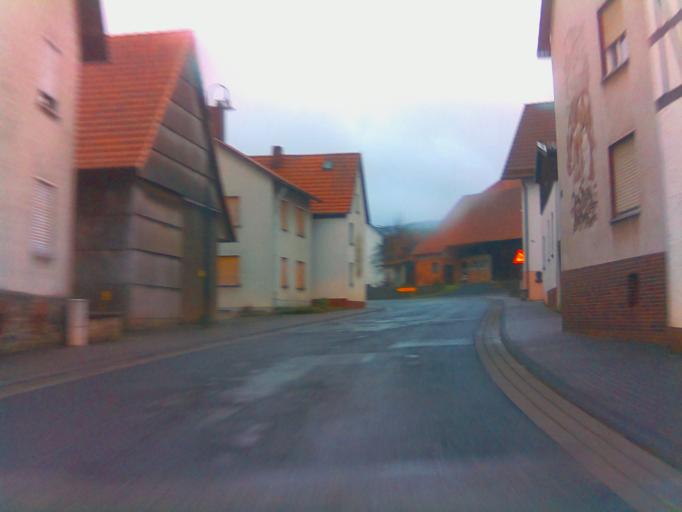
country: DE
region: Thuringia
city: Birx
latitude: 50.5000
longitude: 10.0047
